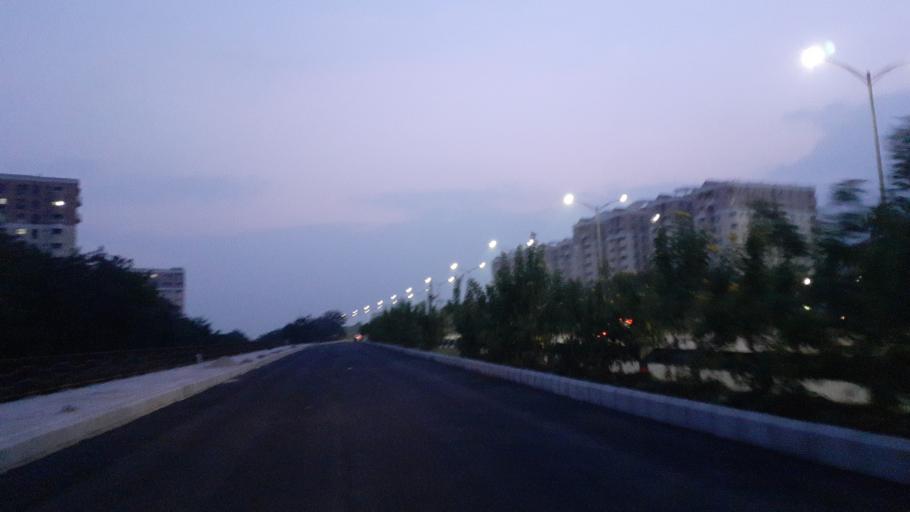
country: IN
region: Telangana
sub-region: Rangareddi
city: Kukatpalli
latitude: 17.4358
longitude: 78.3620
